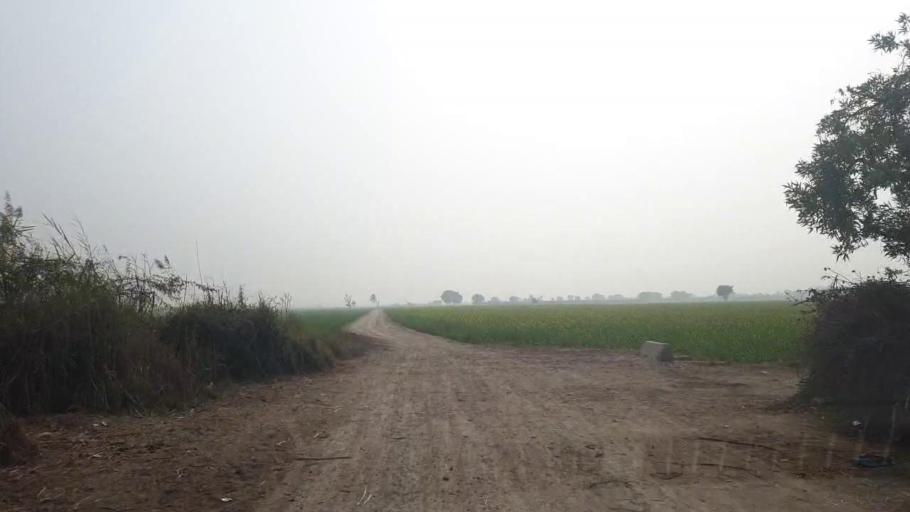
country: PK
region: Sindh
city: Tando Adam
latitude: 25.8194
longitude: 68.5972
